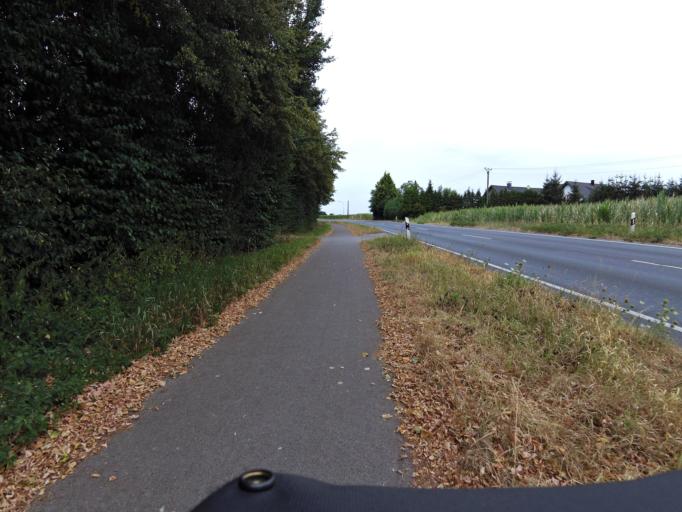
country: DE
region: North Rhine-Westphalia
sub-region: Regierungsbezirk Dusseldorf
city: Weeze
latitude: 51.5792
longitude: 6.1806
